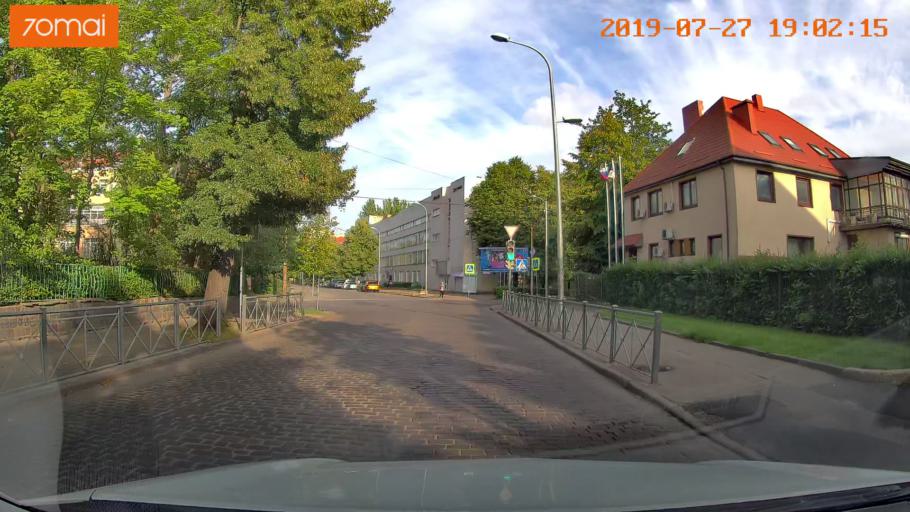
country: RU
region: Kaliningrad
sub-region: Gorod Kaliningrad
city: Kaliningrad
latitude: 54.7249
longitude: 20.4933
